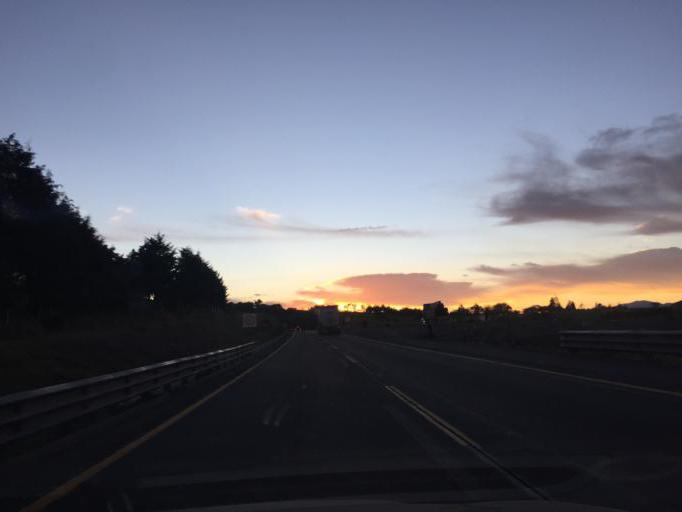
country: MX
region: Puebla
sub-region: Esperanza
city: San Jose Cuyachapa
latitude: 18.8319
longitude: -97.3283
